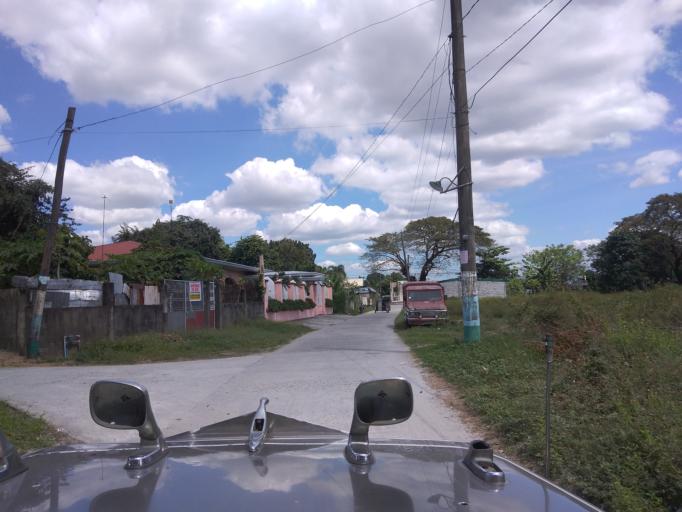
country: PH
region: Central Luzon
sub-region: Province of Pampanga
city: Santa Rita
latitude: 15.0087
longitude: 120.5945
